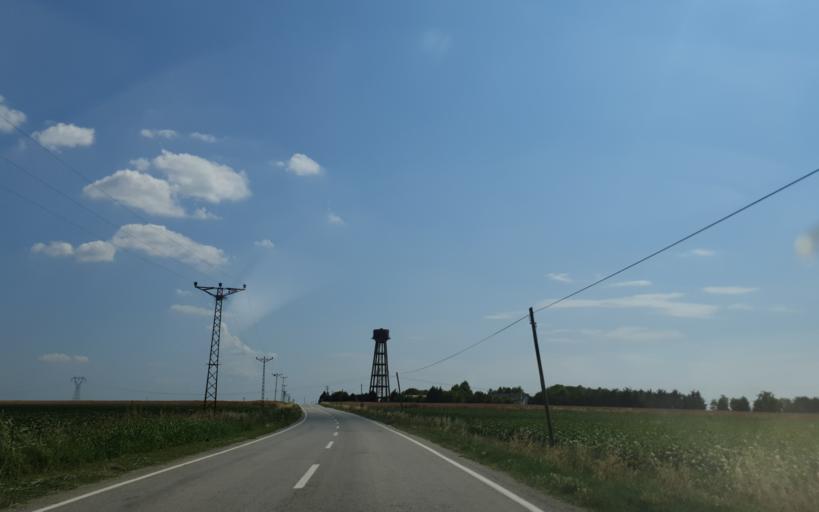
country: TR
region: Kirklareli
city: Buyukkaristiran
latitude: 41.3471
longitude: 27.5482
